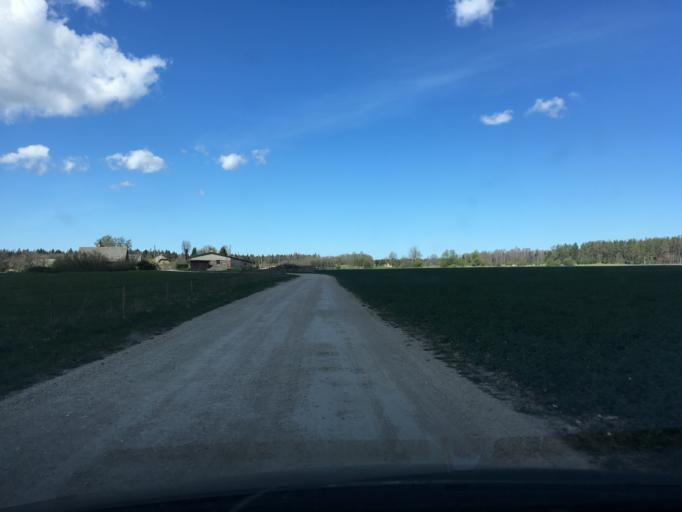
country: EE
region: Harju
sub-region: Raasiku vald
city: Raasiku
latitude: 59.2151
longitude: 25.1647
